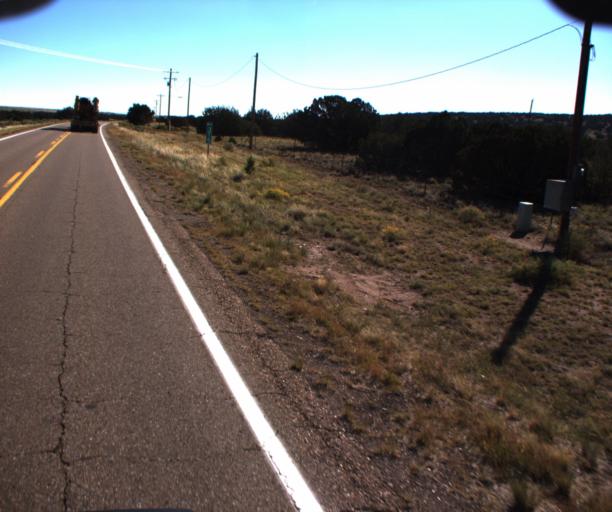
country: US
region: Arizona
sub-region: Apache County
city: Saint Johns
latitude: 34.4839
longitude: -109.5608
